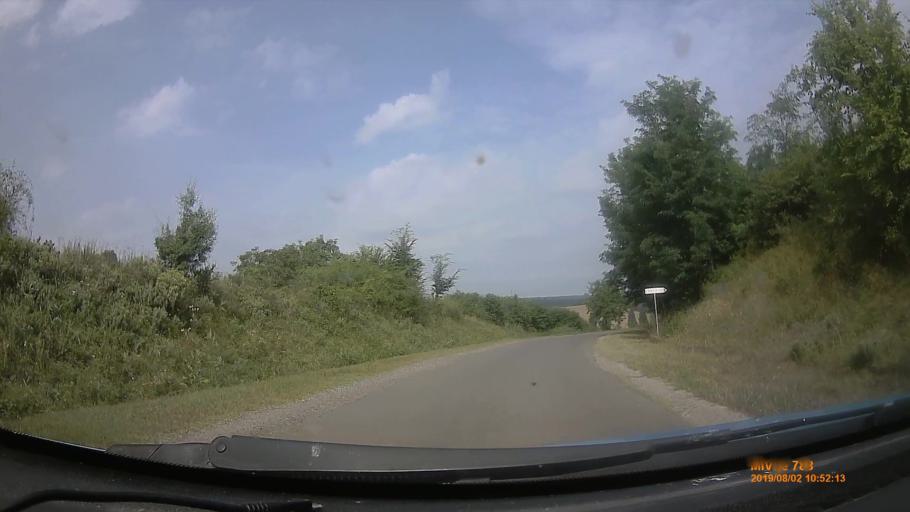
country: HU
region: Baranya
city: Buekkoesd
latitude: 46.0887
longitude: 17.9609
